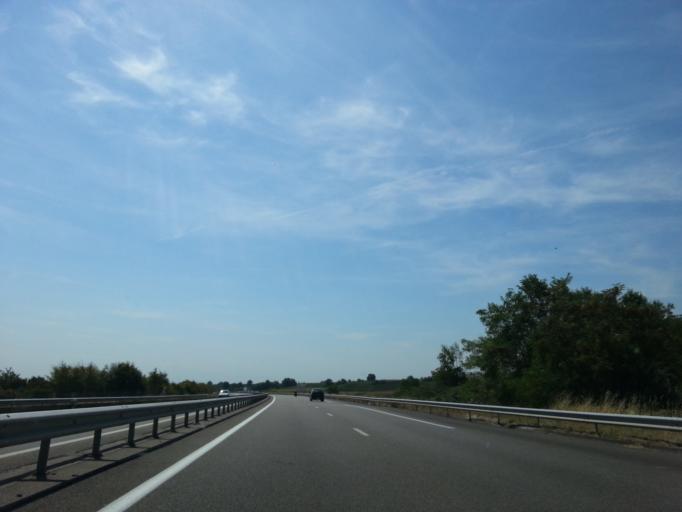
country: FR
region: Alsace
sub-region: Departement du Bas-Rhin
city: Stotzheim
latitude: 48.3770
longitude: 7.4802
